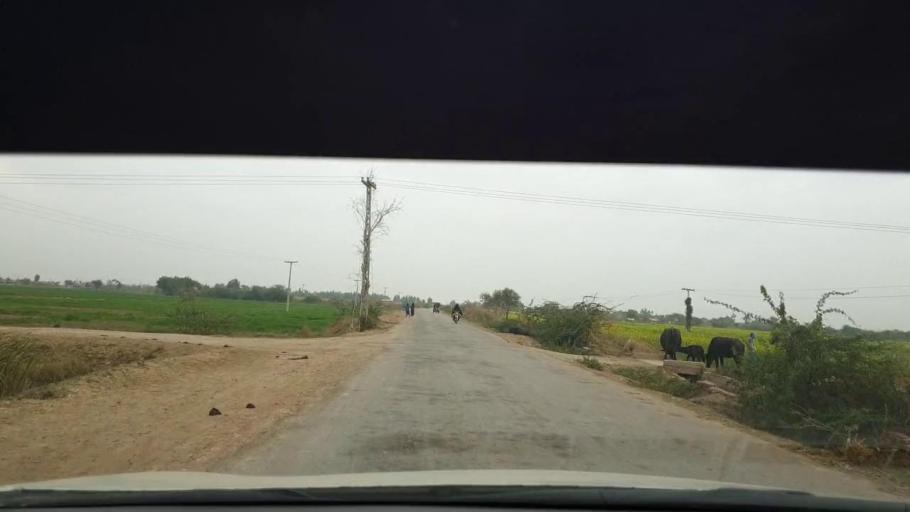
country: PK
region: Sindh
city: Berani
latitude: 25.7766
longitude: 68.8806
